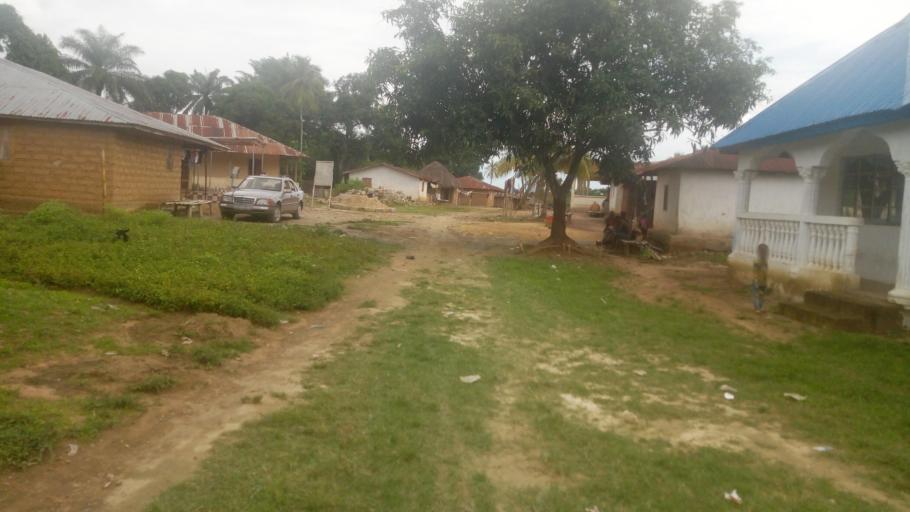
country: SL
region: Northern Province
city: Magburaka
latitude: 8.6793
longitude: -12.0305
